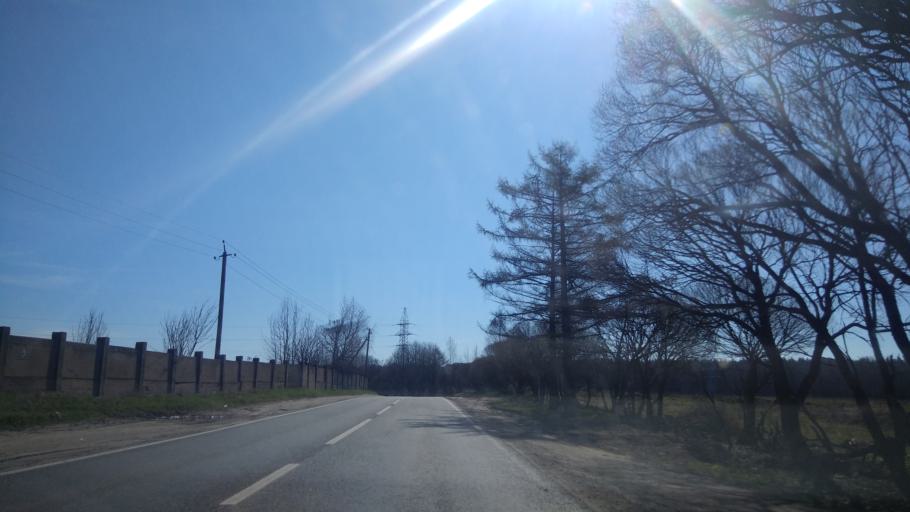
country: RU
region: Moskovskaya
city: Pravdinskiy
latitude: 56.0441
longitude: 37.8872
